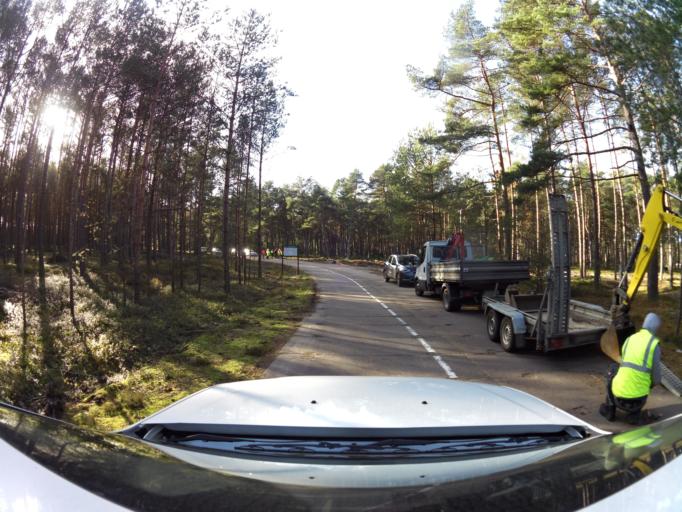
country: PL
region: West Pomeranian Voivodeship
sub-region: Powiat gryficki
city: Cerkwica
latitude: 54.1096
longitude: 15.1490
